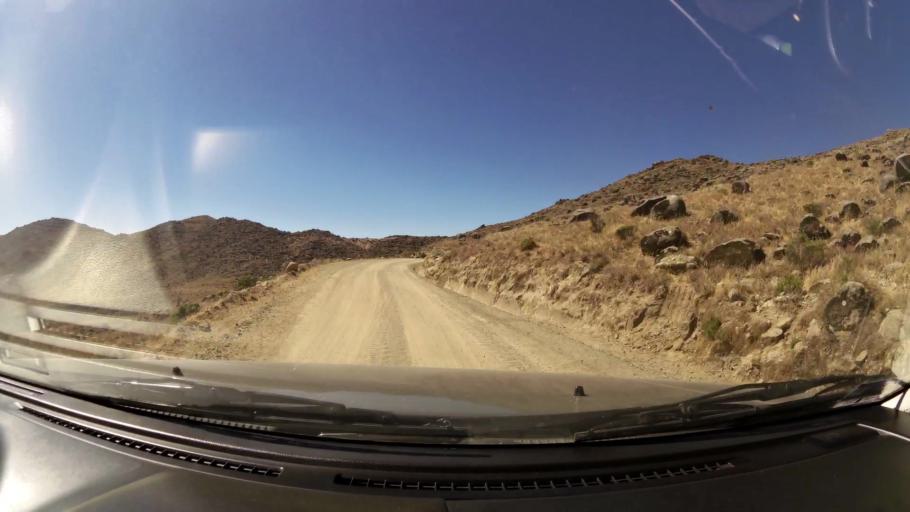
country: PE
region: Huancavelica
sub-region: Huaytara
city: Quito-Arma
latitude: -13.6328
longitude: -75.3616
